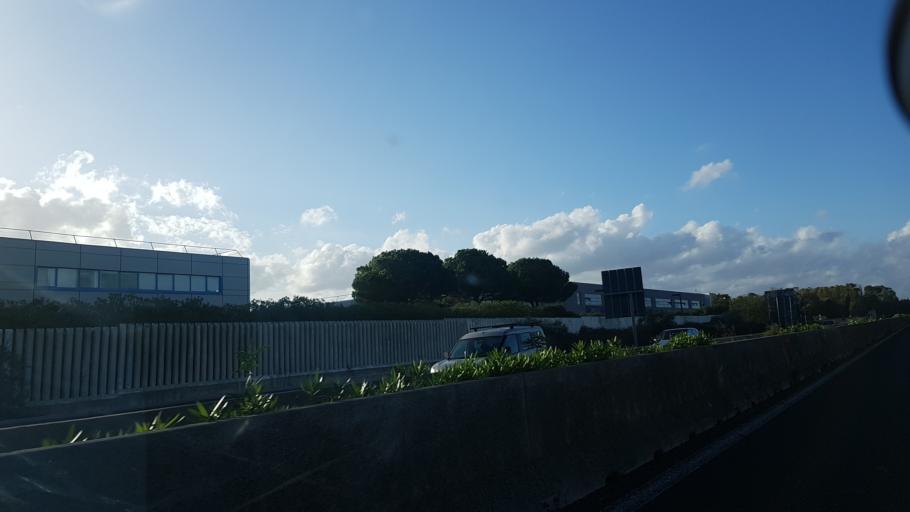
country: IT
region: Apulia
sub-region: Provincia di Lecce
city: Giorgilorio
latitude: 40.3750
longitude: 18.1422
